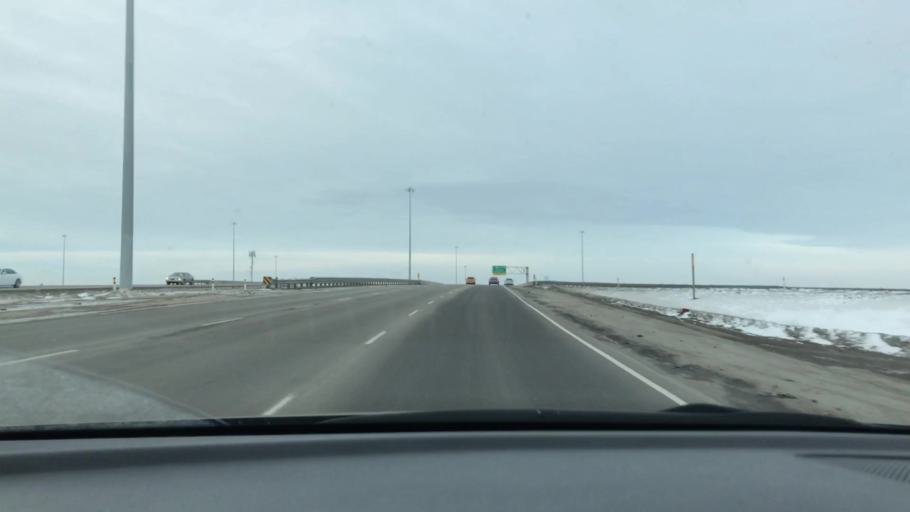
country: CA
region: Alberta
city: Sherwood Park
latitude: 53.5126
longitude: -113.3410
